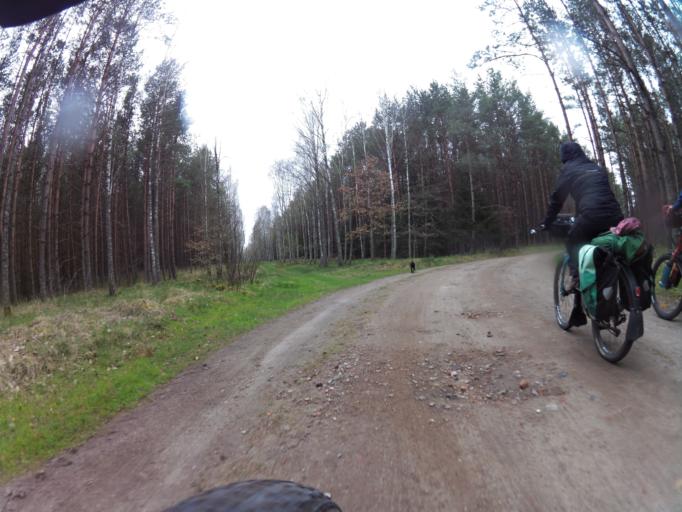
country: PL
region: West Pomeranian Voivodeship
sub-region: Powiat koszalinski
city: Bobolice
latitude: 54.0423
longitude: 16.6177
